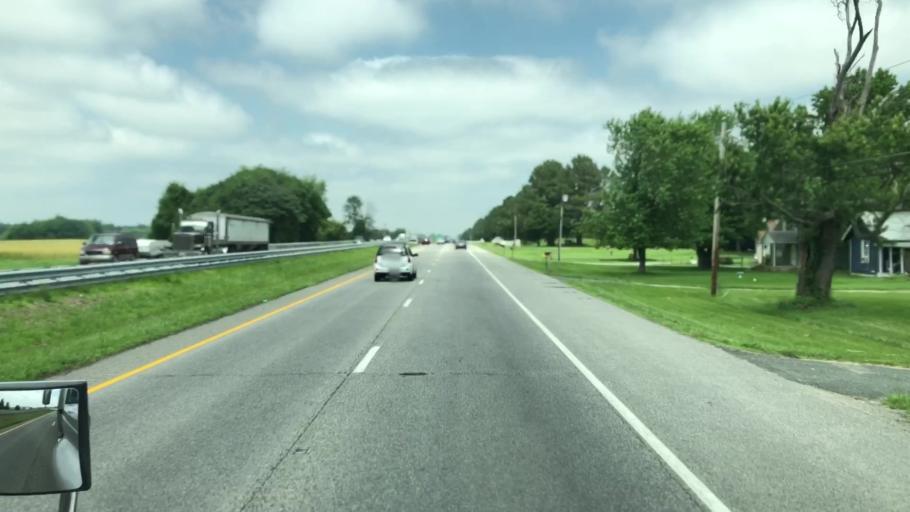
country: US
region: Maryland
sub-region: Talbot County
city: Easton
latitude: 38.8181
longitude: -76.0600
